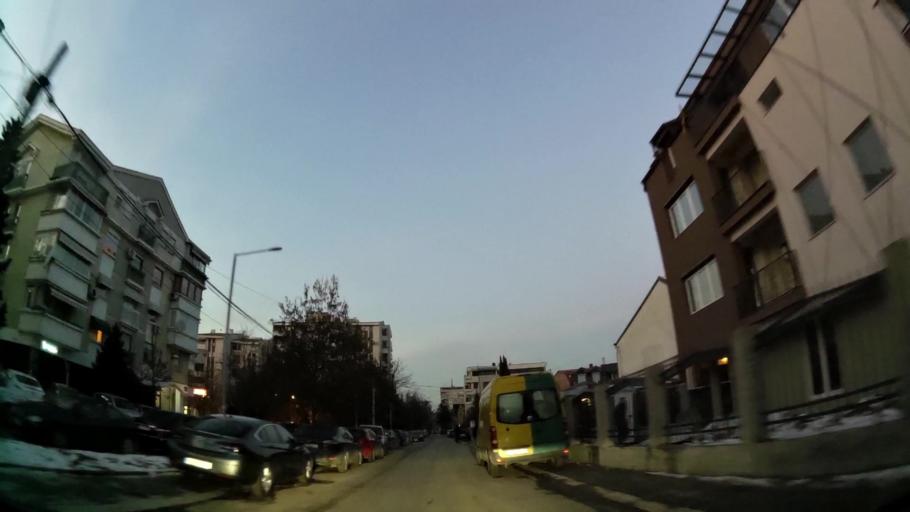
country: MK
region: Karpos
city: Skopje
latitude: 41.9985
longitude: 21.4062
